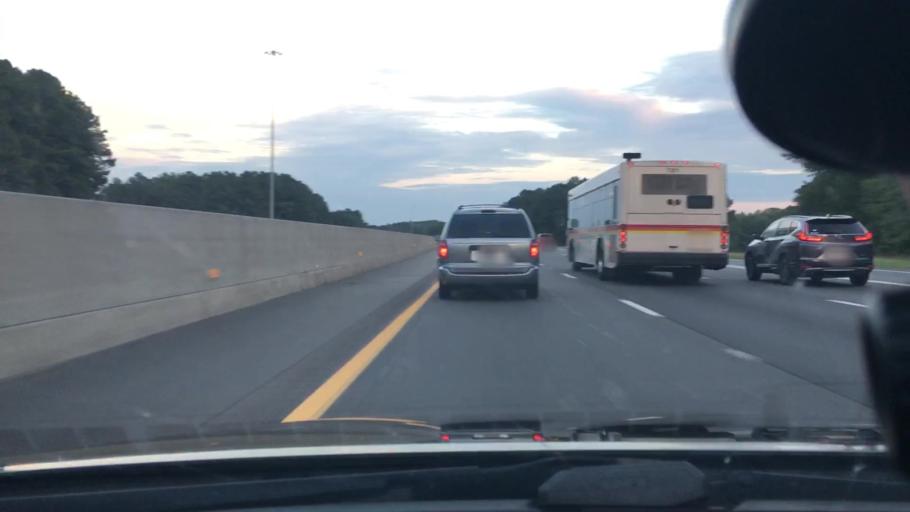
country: US
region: North Carolina
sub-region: Wake County
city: West Raleigh
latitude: 35.7515
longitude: -78.7061
